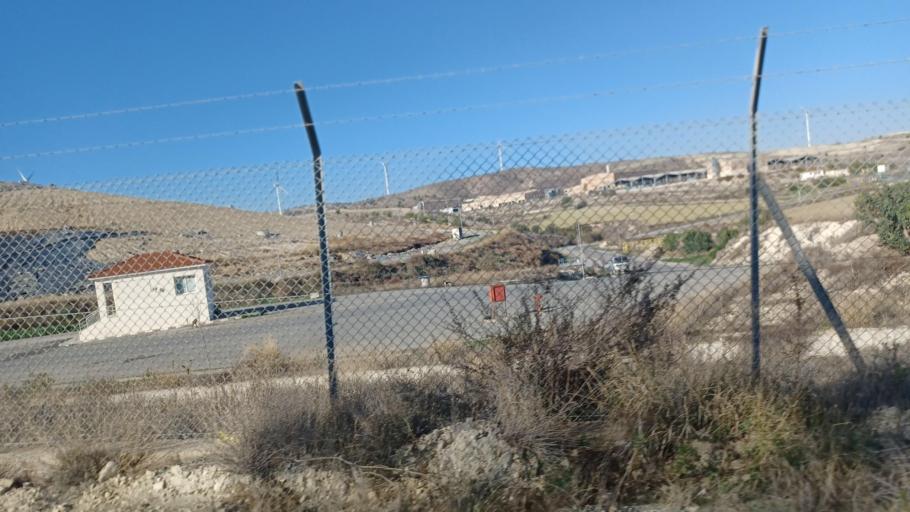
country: CY
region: Larnaka
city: Psevdas
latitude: 34.9638
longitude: 33.5122
